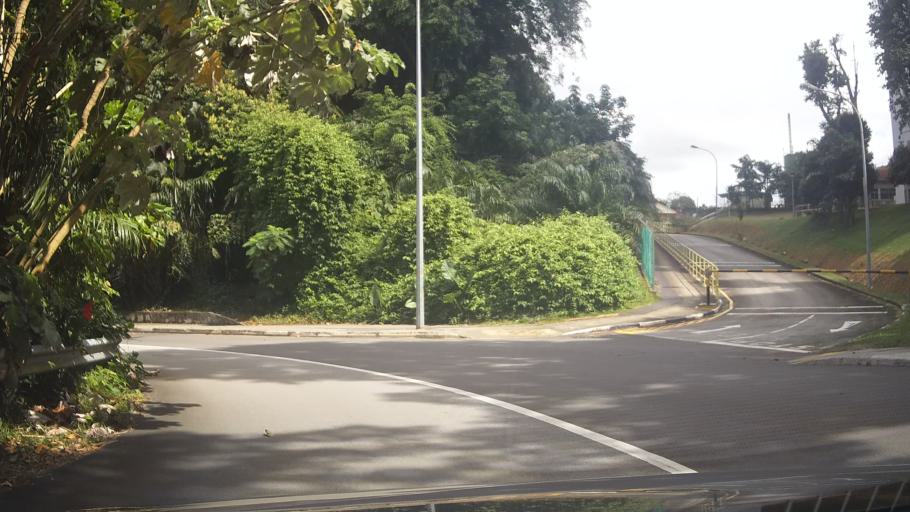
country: MY
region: Johor
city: Johor Bahru
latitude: 1.4469
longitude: 103.7713
